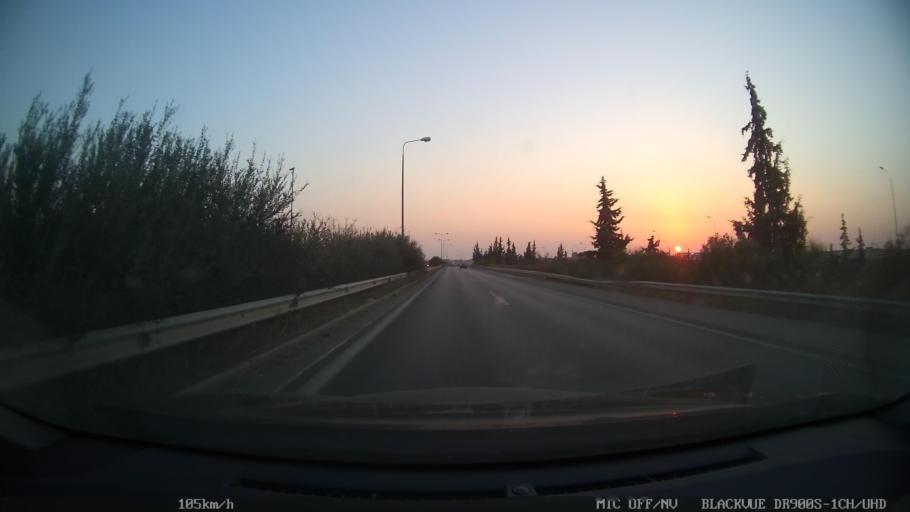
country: GR
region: Central Macedonia
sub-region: Nomos Thessalonikis
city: Pylaia
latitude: 40.5820
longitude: 22.9777
